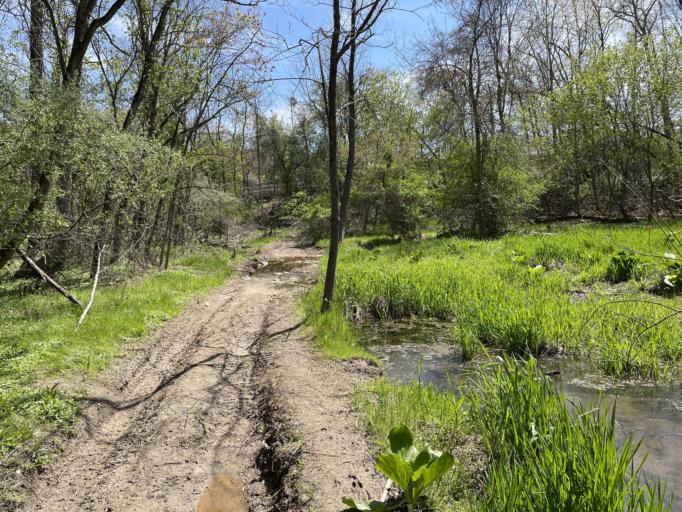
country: US
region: Maryland
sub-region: Baltimore County
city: Owings Mills
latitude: 39.4291
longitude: -76.7774
